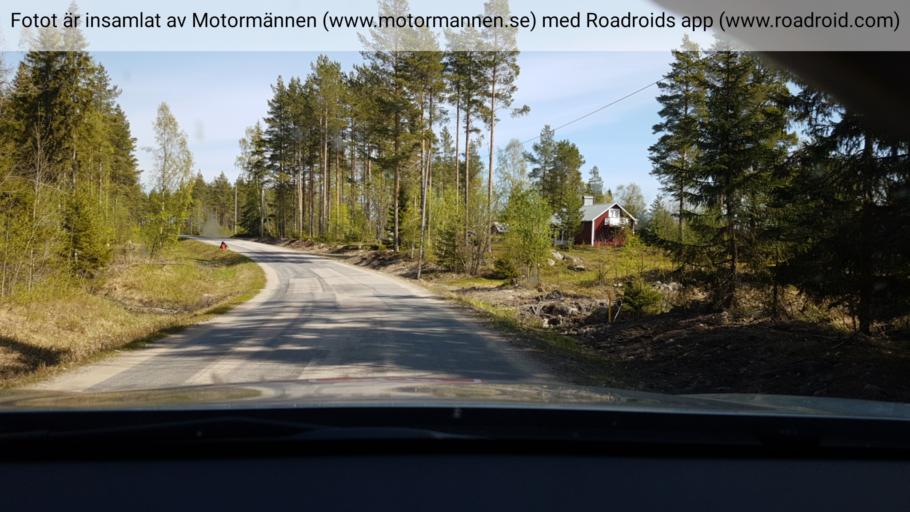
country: SE
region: Vaesterbotten
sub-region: Umea Kommun
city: Saevar
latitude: 63.8090
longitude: 20.5822
